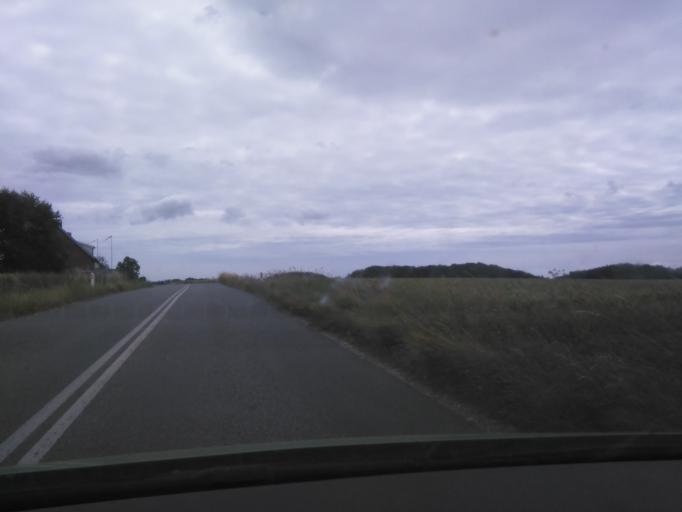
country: DK
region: Central Jutland
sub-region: Odder Kommune
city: Odder
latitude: 55.9918
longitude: 10.1271
